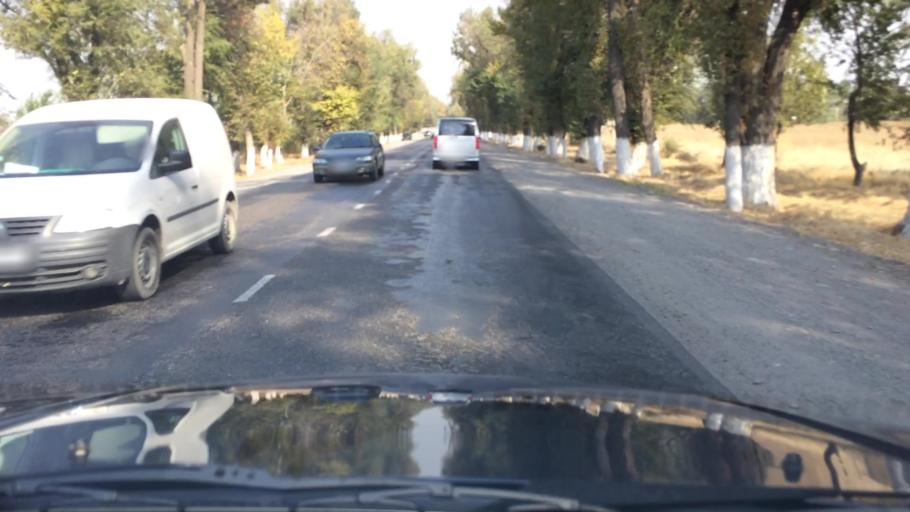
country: KG
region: Chuy
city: Lebedinovka
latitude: 42.9273
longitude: 74.6908
